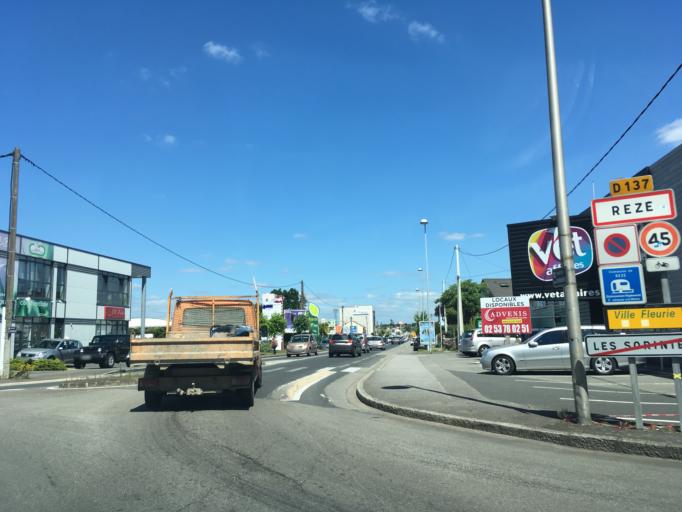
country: FR
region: Pays de la Loire
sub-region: Departement de la Loire-Atlantique
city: Les Sorinieres
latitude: 47.1523
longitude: -1.5350
